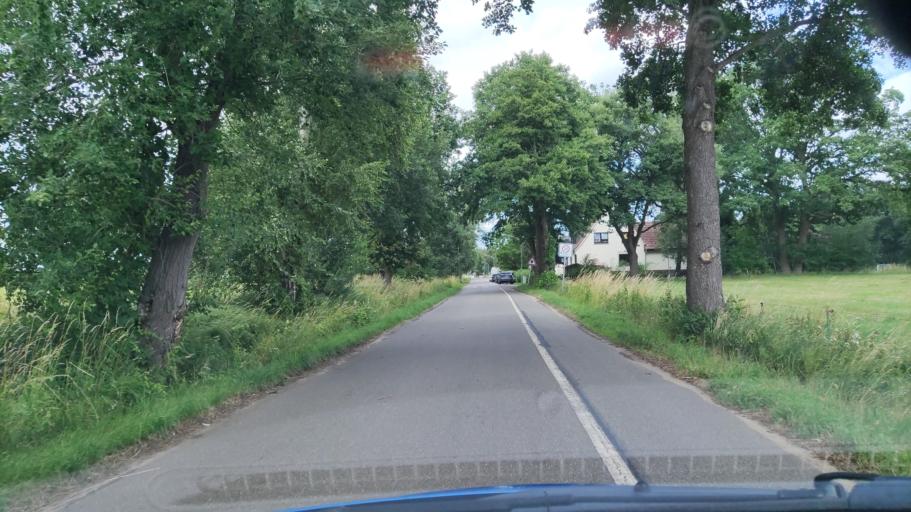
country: DE
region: Lower Saxony
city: Stelle
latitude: 53.4169
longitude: 10.0709
